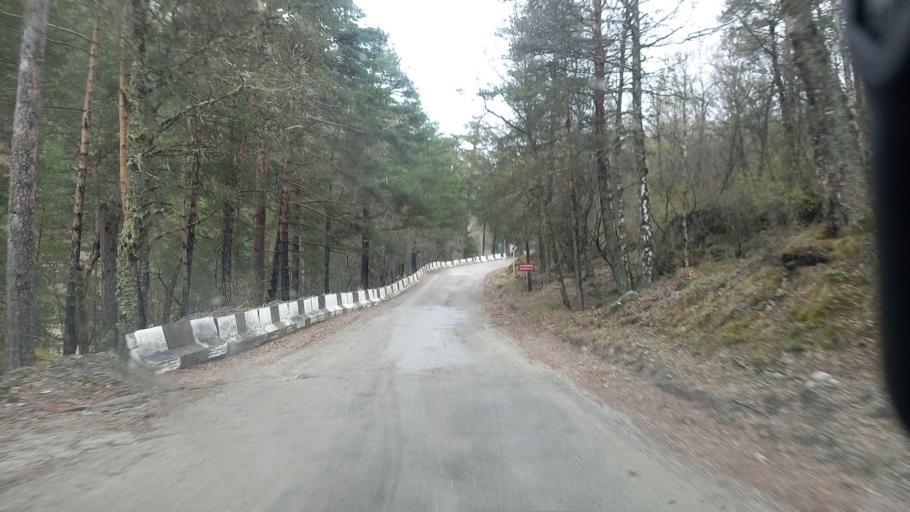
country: RU
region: Kabardino-Balkariya
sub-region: El'brusskiy Rayon
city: El'brus
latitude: 43.2349
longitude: 42.6476
